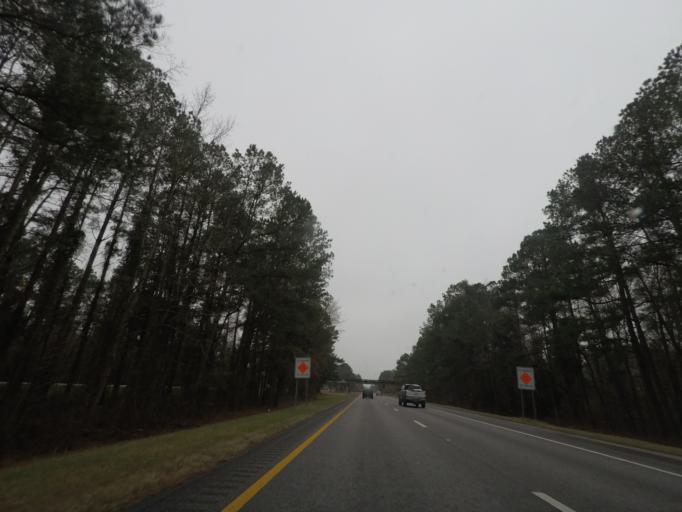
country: US
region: South Carolina
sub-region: Sumter County
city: East Sumter
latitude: 33.8882
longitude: -80.0988
